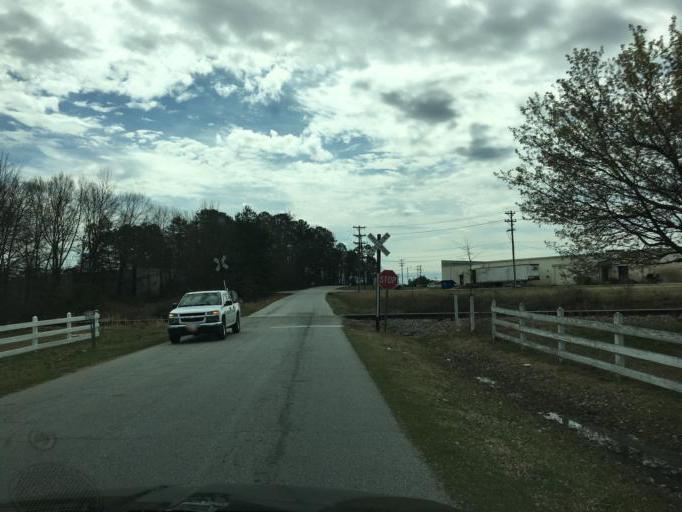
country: US
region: South Carolina
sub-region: Greenville County
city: Fountain Inn
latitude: 34.6941
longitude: -82.2223
